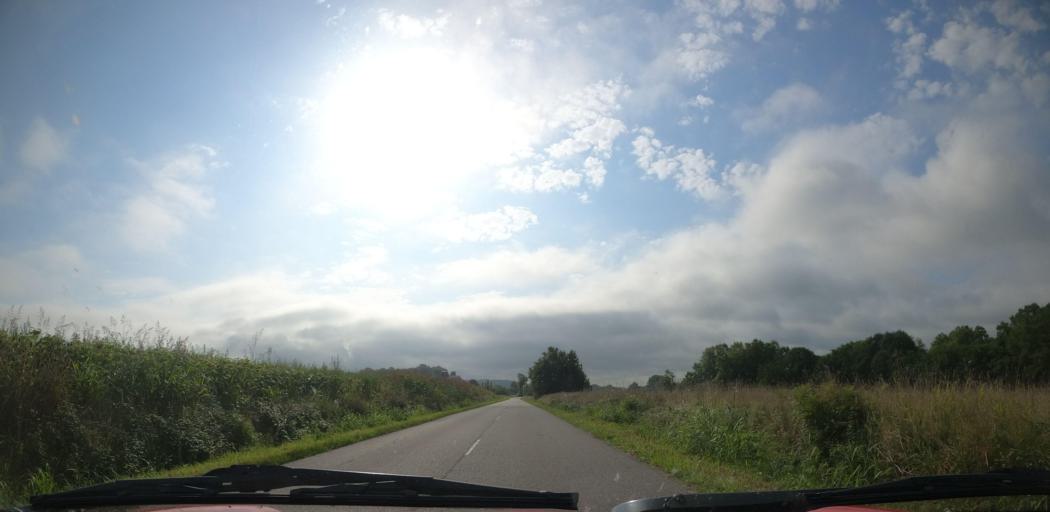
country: FR
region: Aquitaine
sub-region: Departement des Landes
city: Peyrehorade
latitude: 43.5361
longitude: -1.0735
